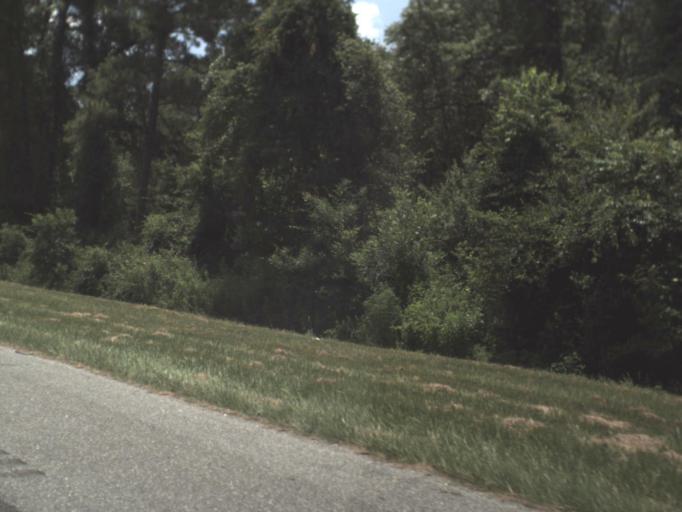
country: US
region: Florida
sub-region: Madison County
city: Madison
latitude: 30.4364
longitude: -83.6482
